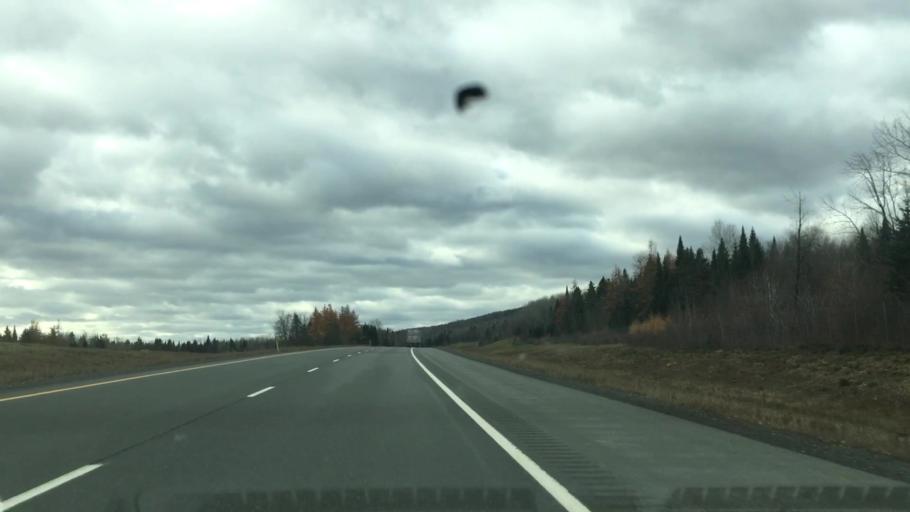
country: US
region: Maine
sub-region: Aroostook County
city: Fort Fairfield
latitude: 46.6580
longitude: -67.7345
